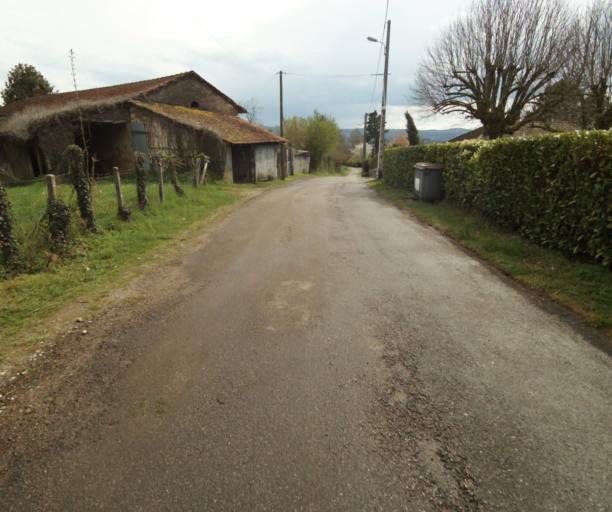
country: FR
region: Limousin
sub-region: Departement de la Correze
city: Tulle
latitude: 45.2675
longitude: 1.7551
